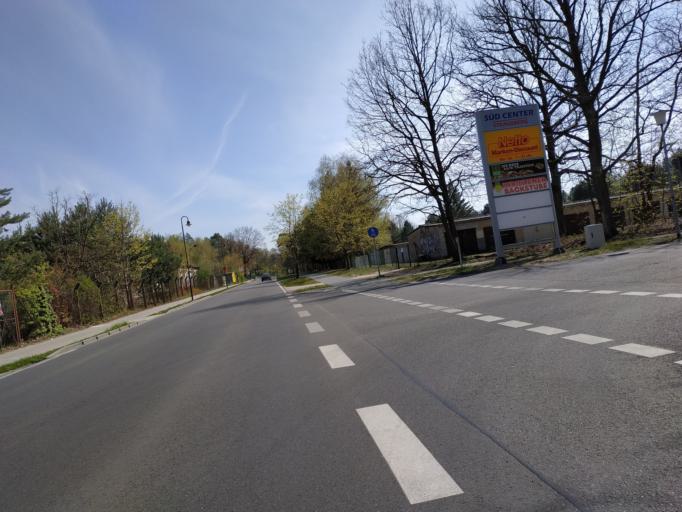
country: DE
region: Brandenburg
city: Petershagen
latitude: 52.5389
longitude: 13.8346
